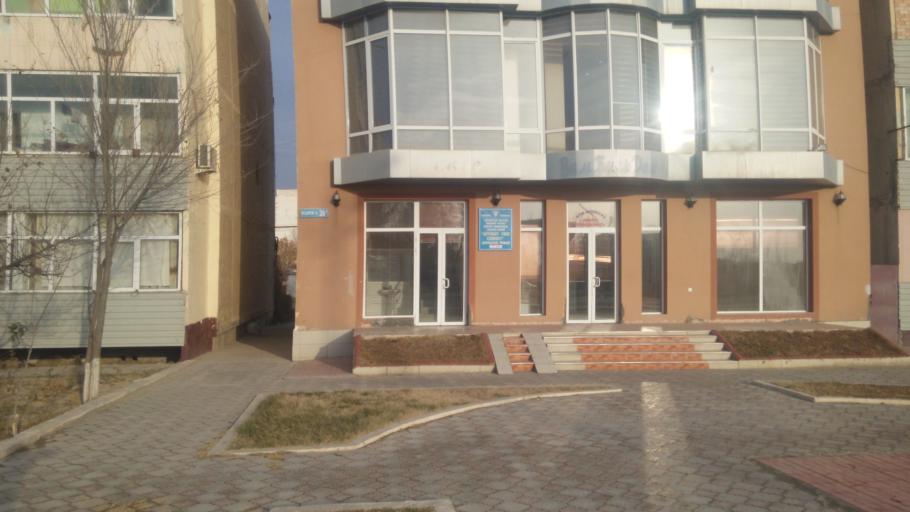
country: UZ
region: Sirdaryo
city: Guliston
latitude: 40.5134
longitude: 68.7821
